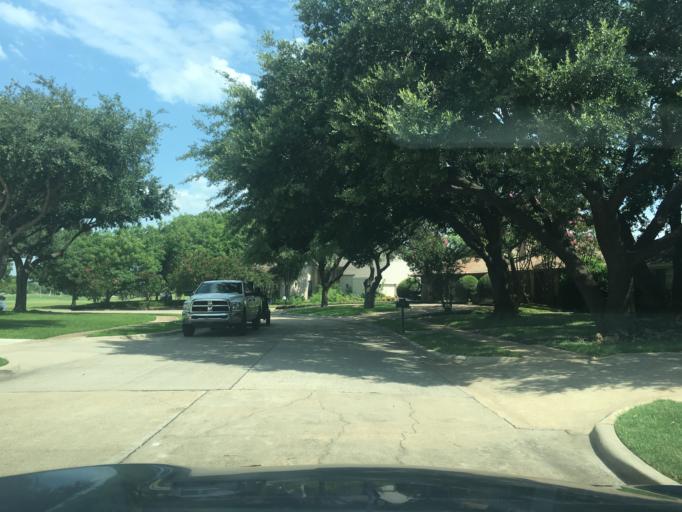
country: US
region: Texas
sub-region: Dallas County
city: Carrollton
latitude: 32.9345
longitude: -96.8595
